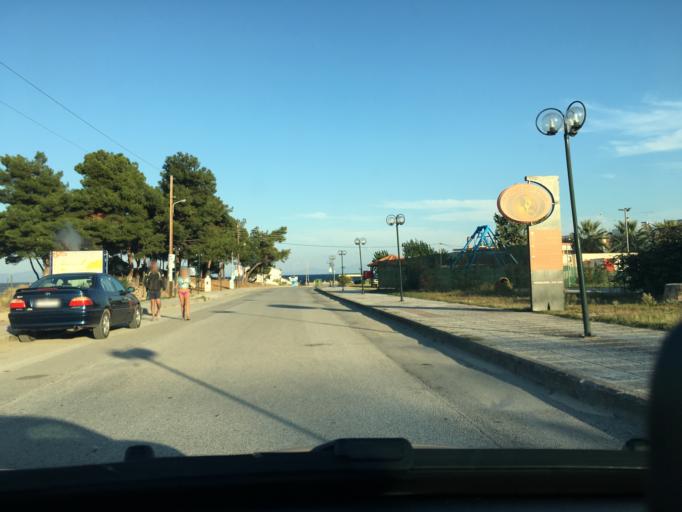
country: GR
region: Central Macedonia
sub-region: Nomos Chalkidikis
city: Nea Potidhaia
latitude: 40.1966
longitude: 23.3312
